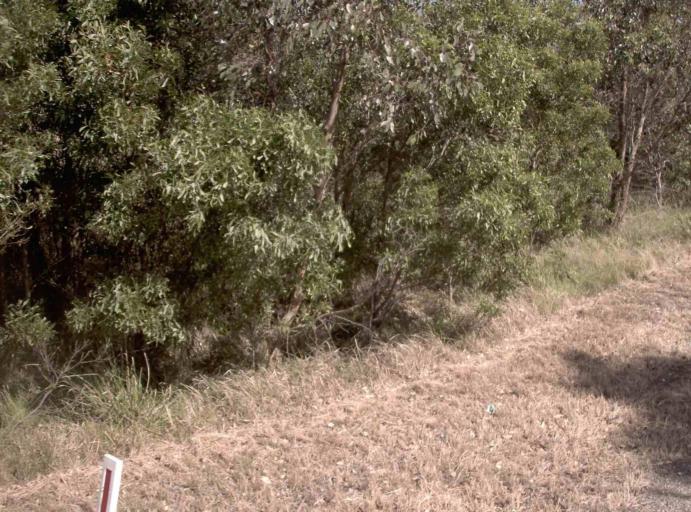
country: AU
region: Victoria
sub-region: Wellington
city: Sale
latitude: -38.3014
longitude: 147.1533
